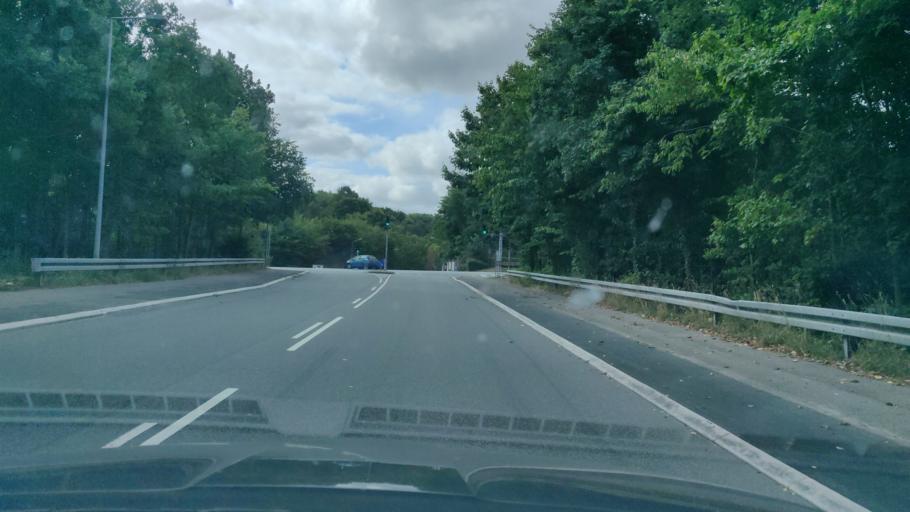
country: DK
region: Capital Region
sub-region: Hoje-Taastrup Kommune
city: Flong
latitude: 55.6485
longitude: 12.1777
